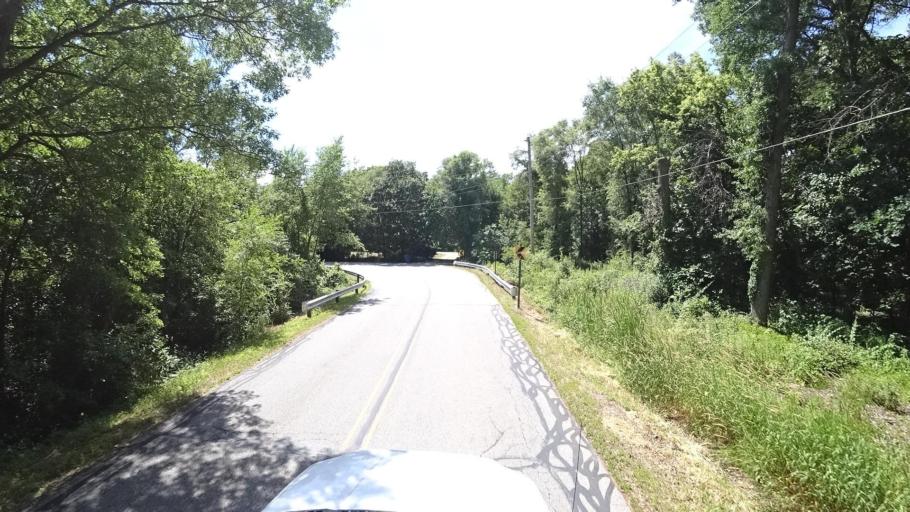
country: US
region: Indiana
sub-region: Porter County
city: Porter
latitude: 41.6067
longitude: -87.0906
